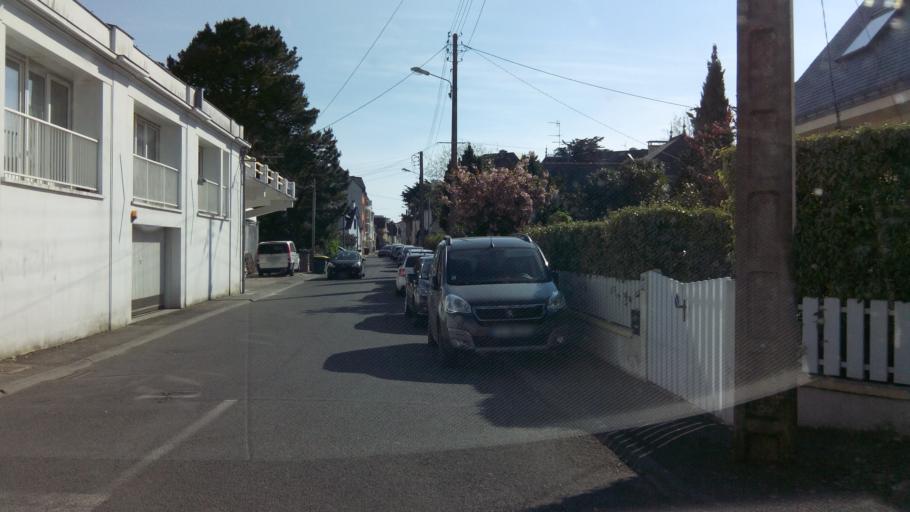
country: FR
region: Pays de la Loire
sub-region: Departement de la Loire-Atlantique
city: Pornichet
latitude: 47.2684
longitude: -2.3405
